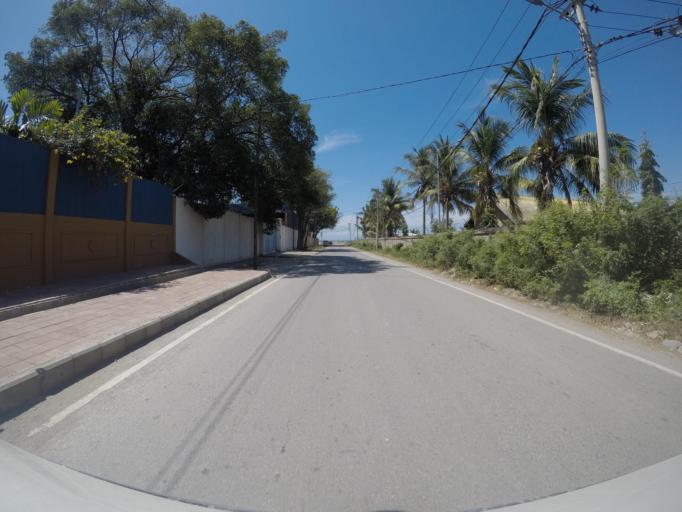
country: TL
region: Dili
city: Dili
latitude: -8.5441
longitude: 125.5457
